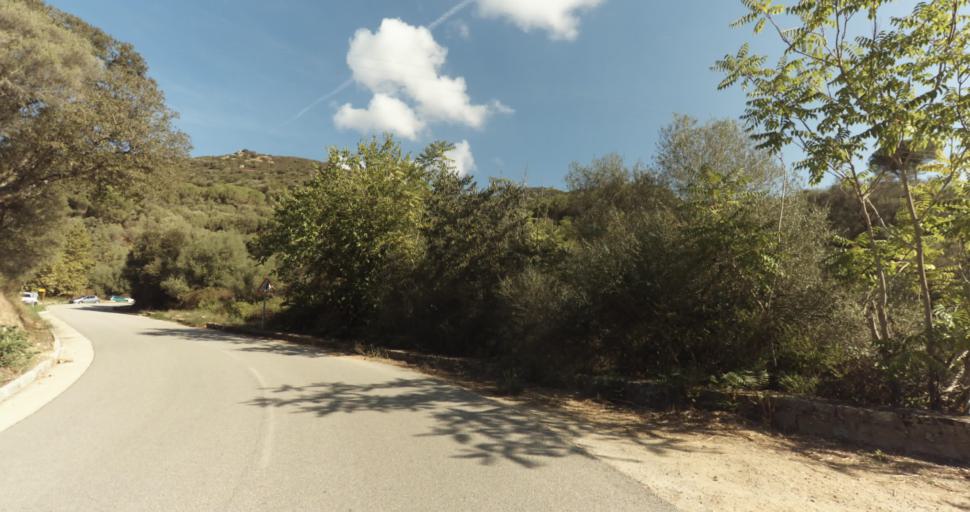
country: FR
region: Corsica
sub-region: Departement de la Corse-du-Sud
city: Ajaccio
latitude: 41.9305
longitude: 8.7023
